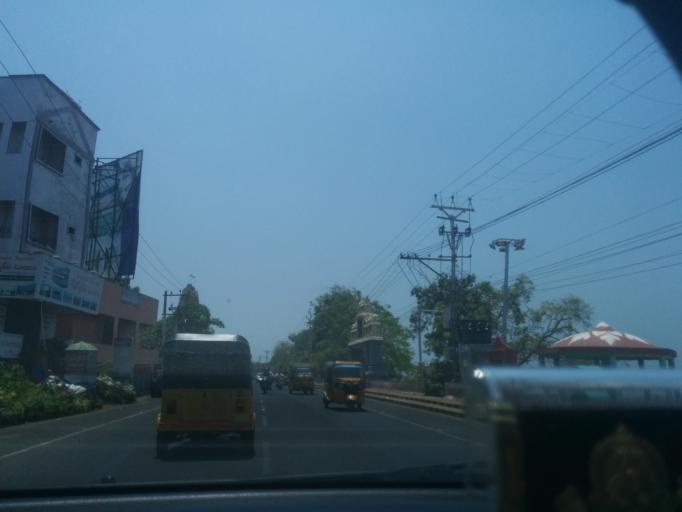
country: IN
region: Andhra Pradesh
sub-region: East Godavari
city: Rajahmundry
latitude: 17.0037
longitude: 81.7670
